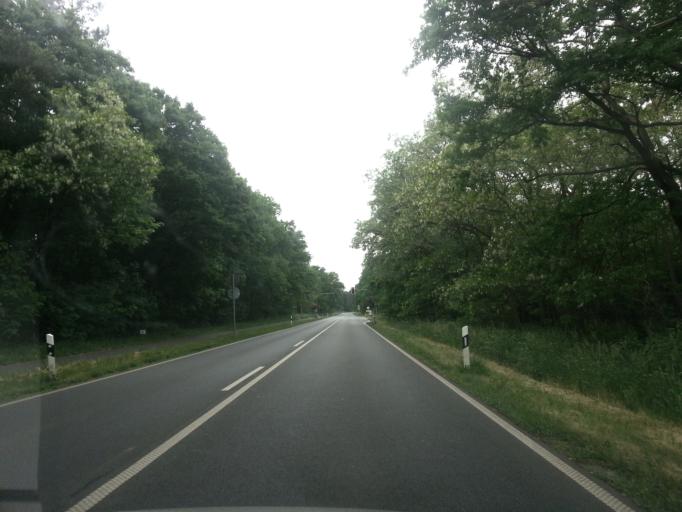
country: DE
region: Hesse
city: Pfungstadt
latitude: 49.8389
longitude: 8.6022
